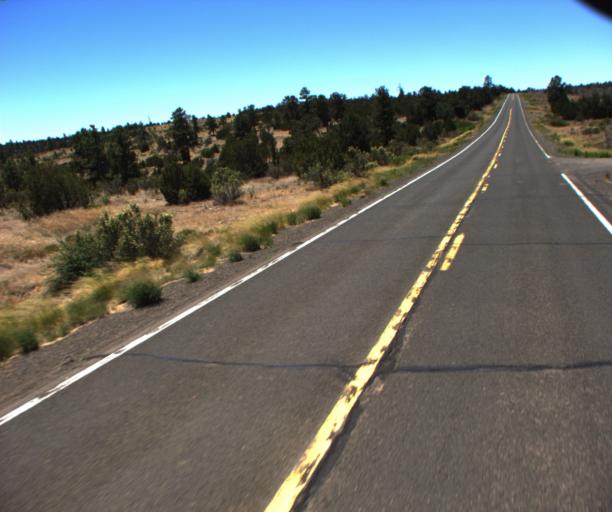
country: US
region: Arizona
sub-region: Coconino County
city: LeChee
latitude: 34.7183
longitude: -111.0898
